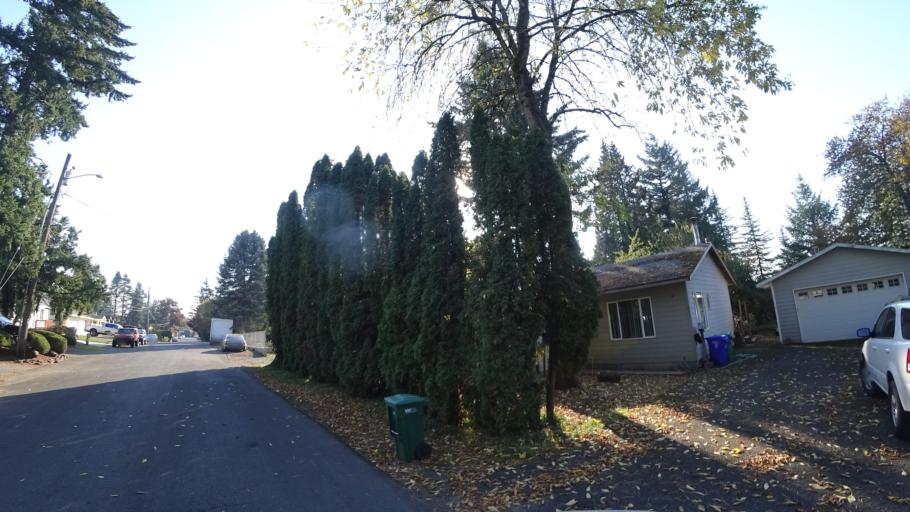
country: US
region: Oregon
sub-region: Multnomah County
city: Fairview
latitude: 45.5218
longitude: -122.4432
